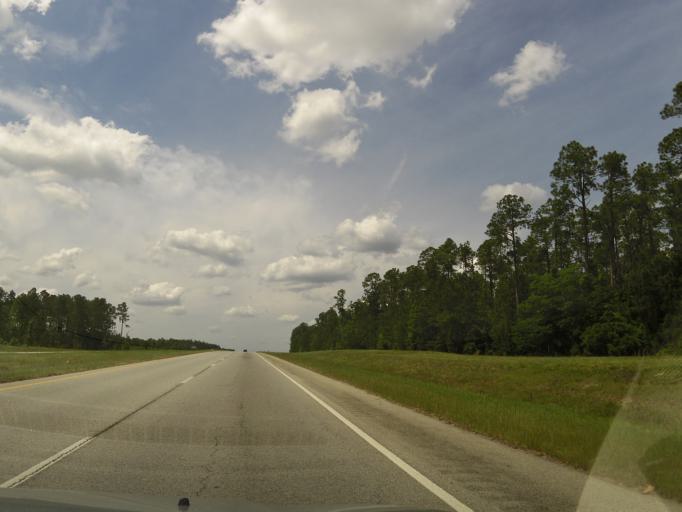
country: US
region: Georgia
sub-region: Emanuel County
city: Swainsboro
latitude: 32.6464
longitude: -82.3672
